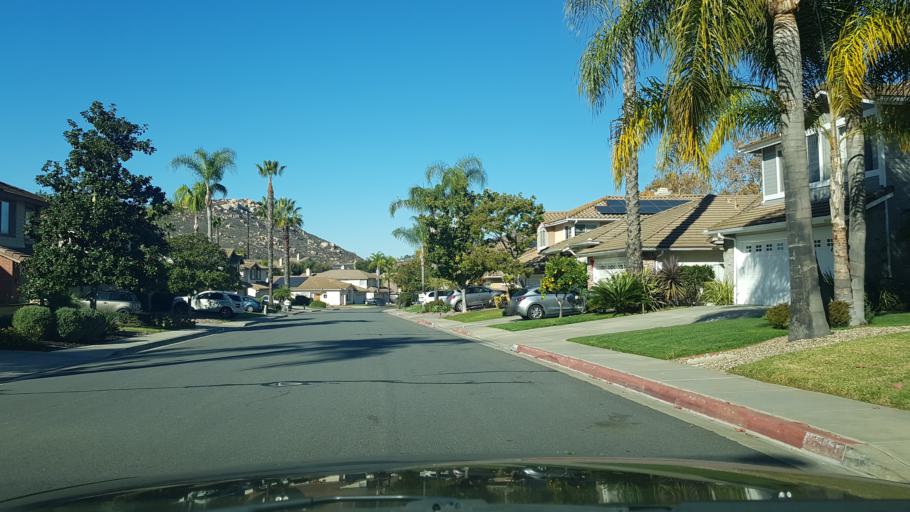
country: US
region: California
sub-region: San Diego County
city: Escondido
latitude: 33.0409
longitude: -117.0890
